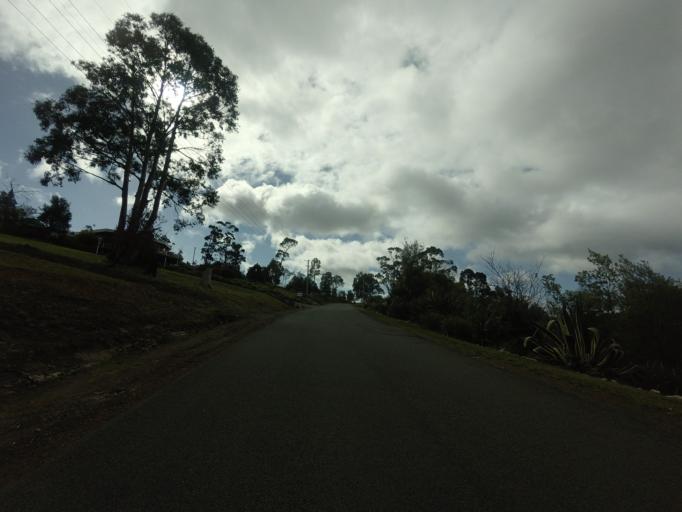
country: AU
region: Tasmania
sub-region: Sorell
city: Sorell
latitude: -42.5404
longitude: 147.9108
